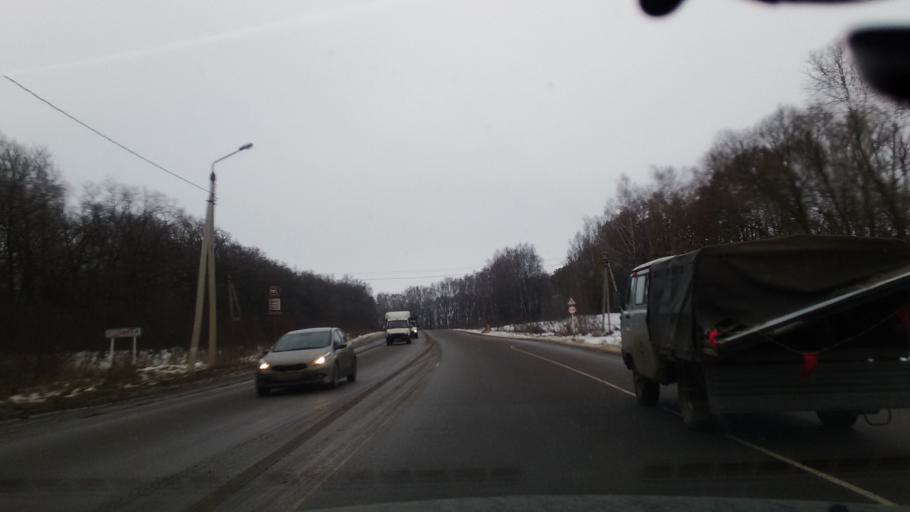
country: RU
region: Tula
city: Skuratovskiy
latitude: 54.1294
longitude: 37.6809
